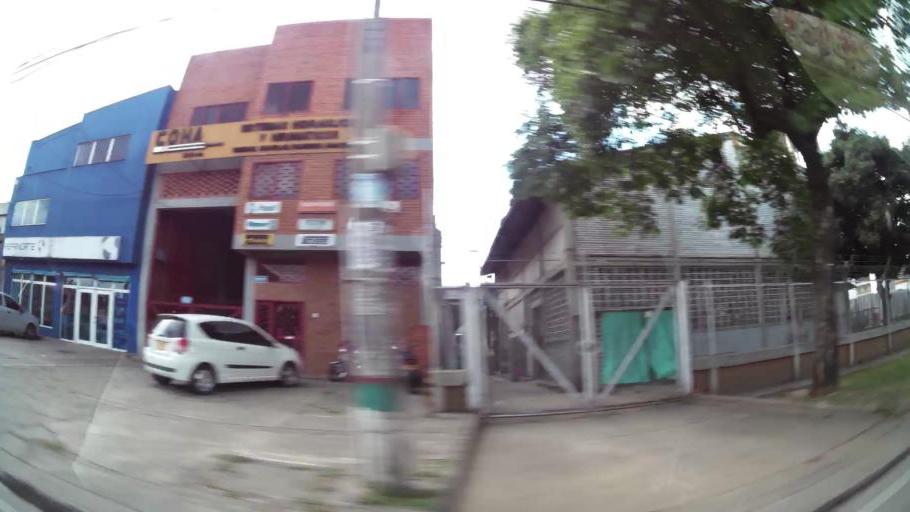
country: CO
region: Valle del Cauca
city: Cali
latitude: 3.4795
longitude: -76.5052
